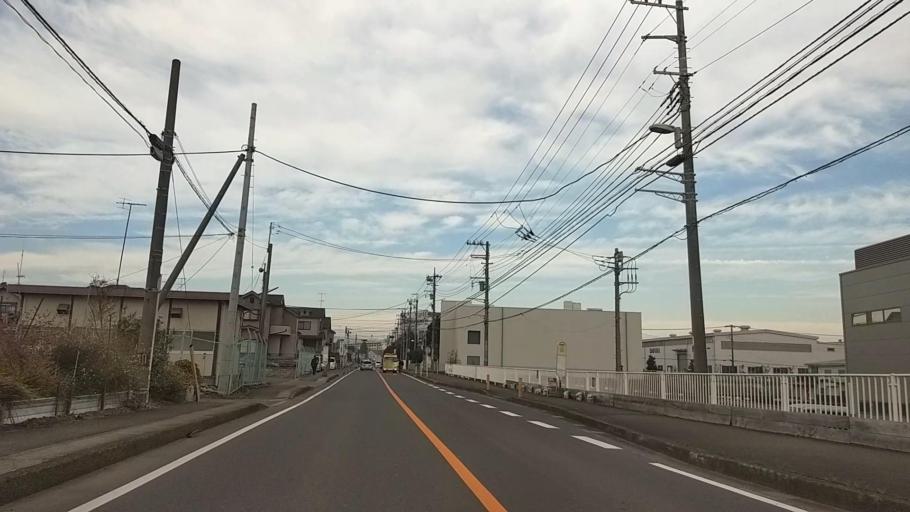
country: JP
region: Kanagawa
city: Fujisawa
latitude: 35.3998
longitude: 139.4272
